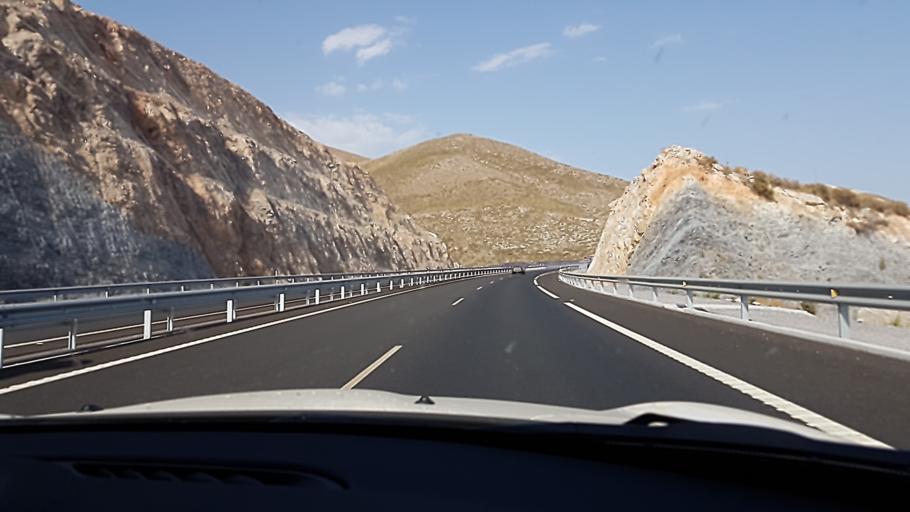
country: ES
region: Andalusia
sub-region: Provincia de Granada
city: Gualchos
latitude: 36.7135
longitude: -3.3987
